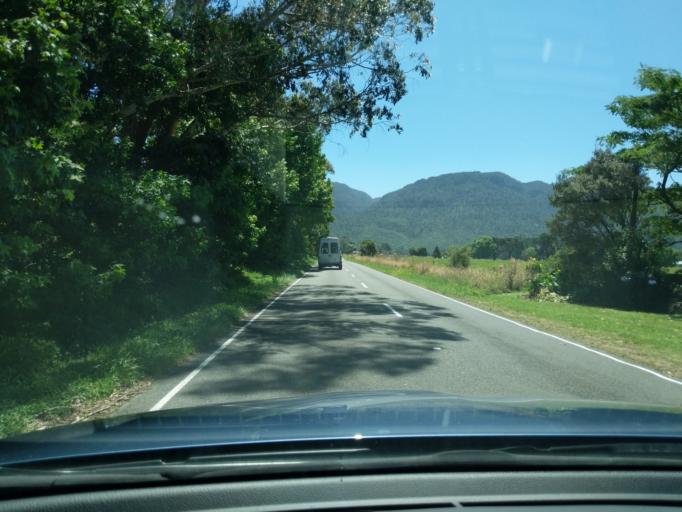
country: NZ
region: Tasman
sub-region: Tasman District
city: Takaka
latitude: -40.7029
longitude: 172.6341
